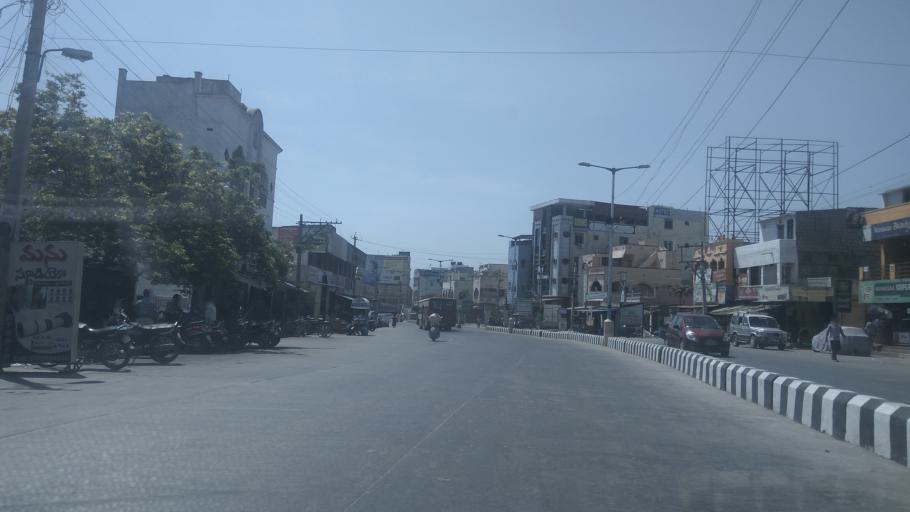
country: IN
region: Andhra Pradesh
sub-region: Chittoor
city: Tirupati
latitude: 13.6090
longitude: 79.4481
